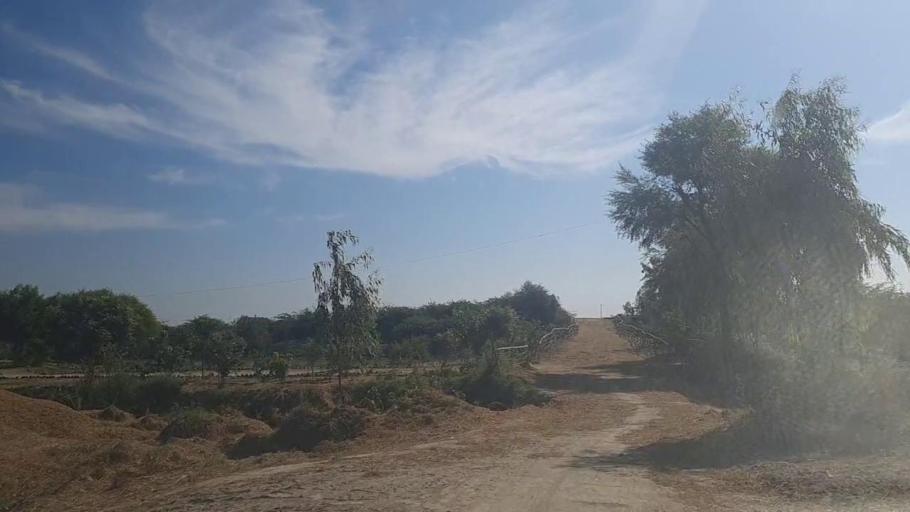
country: PK
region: Sindh
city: Mirpur Batoro
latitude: 24.6539
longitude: 68.2027
